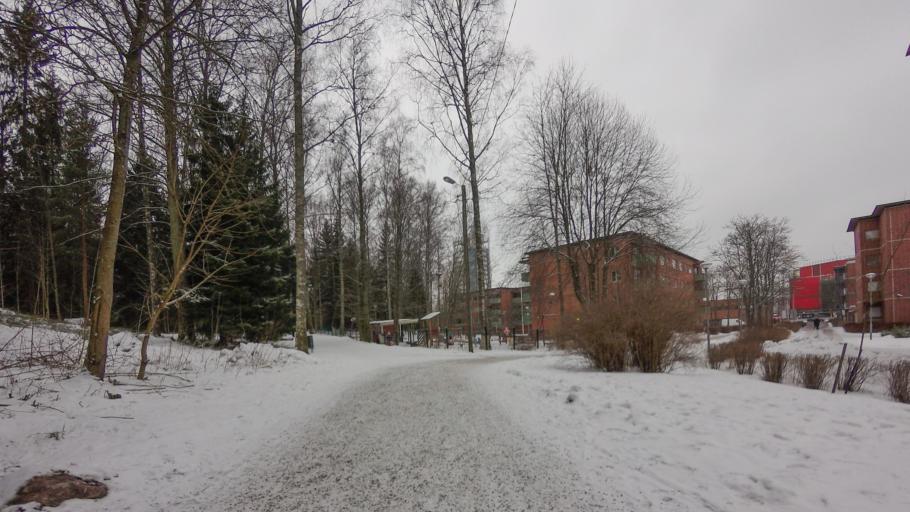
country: FI
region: Uusimaa
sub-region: Helsinki
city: Vantaa
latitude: 60.2076
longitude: 25.0876
